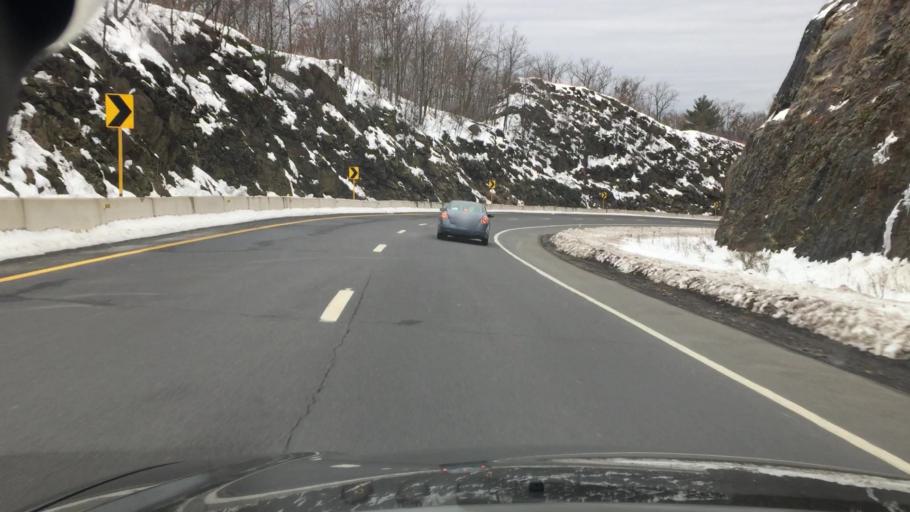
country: US
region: Pennsylvania
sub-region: Luzerne County
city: Ashley
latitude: 41.1876
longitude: -75.8924
